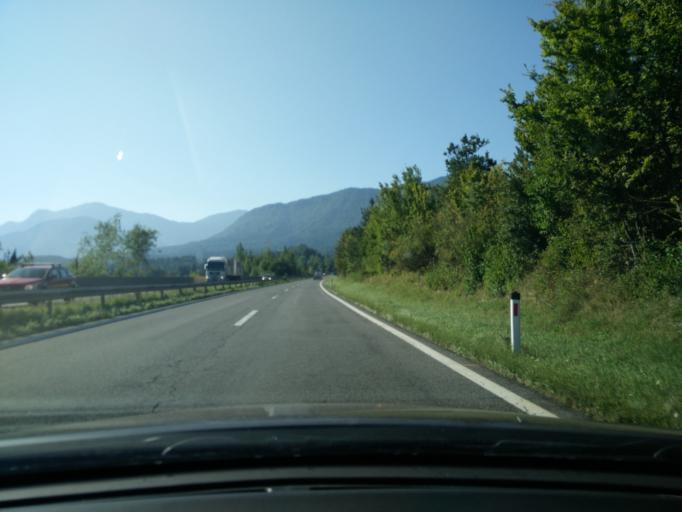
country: AT
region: Carinthia
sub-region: Politischer Bezirk Villach Land
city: Rosegg
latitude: 46.5676
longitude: 14.0064
